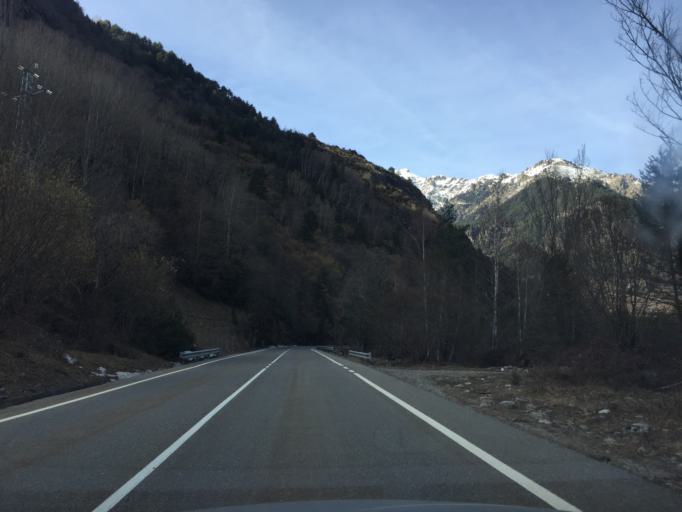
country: ES
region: Aragon
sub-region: Provincia de Huesca
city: Bielsa
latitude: 42.6470
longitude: 0.2108
